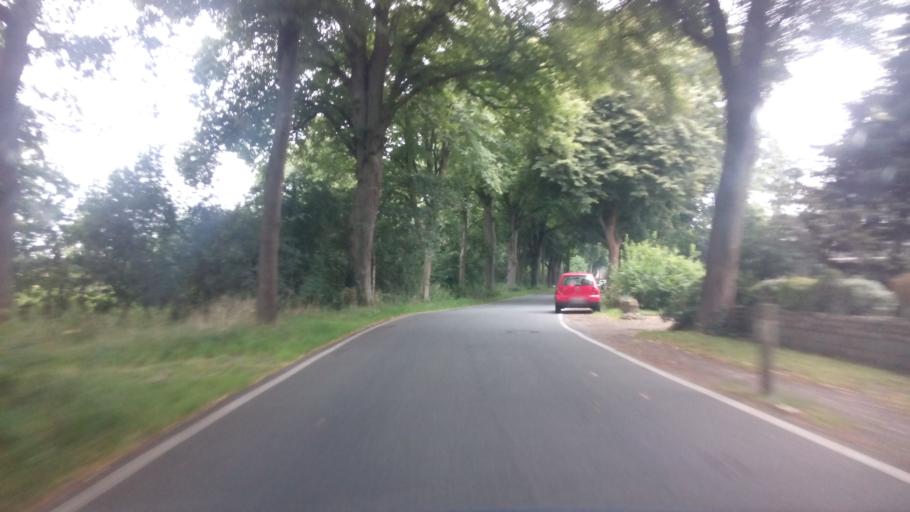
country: DE
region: Lower Saxony
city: Lilienthal
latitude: 53.1235
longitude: 8.8773
